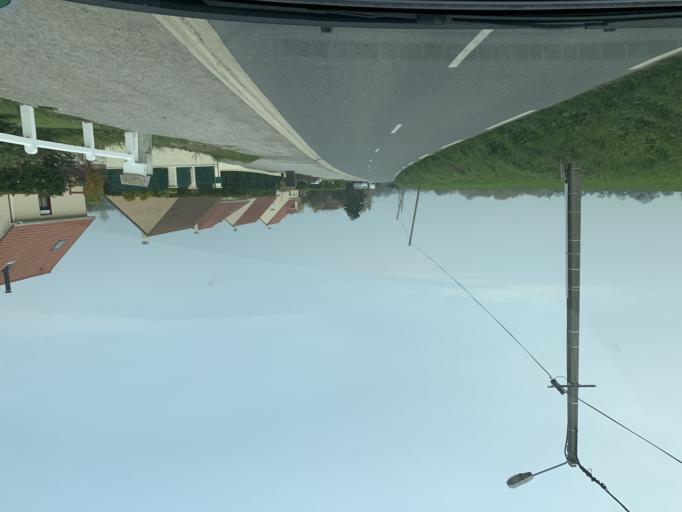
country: FR
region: Nord-Pas-de-Calais
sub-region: Departement du Pas-de-Calais
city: Samer
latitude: 50.6669
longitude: 1.7503
